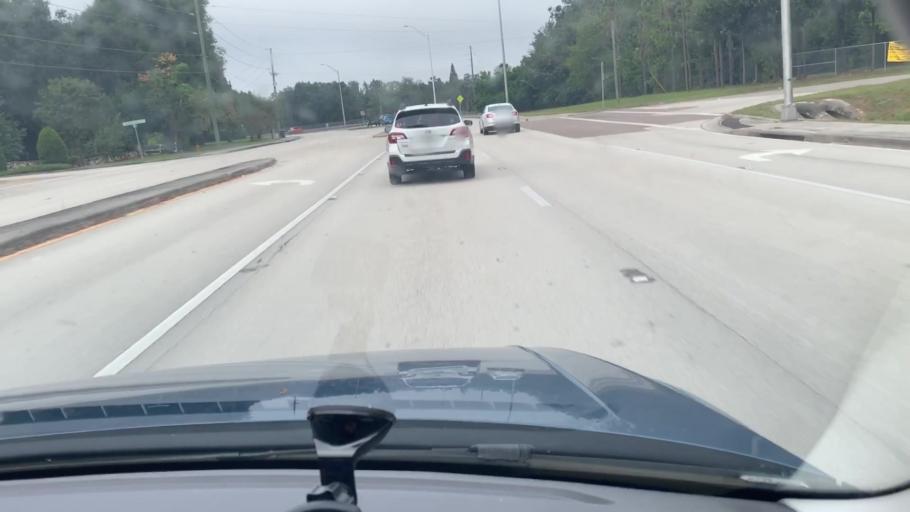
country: US
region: Florida
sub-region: Polk County
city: Gibsonia
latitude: 28.0942
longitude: -81.9978
